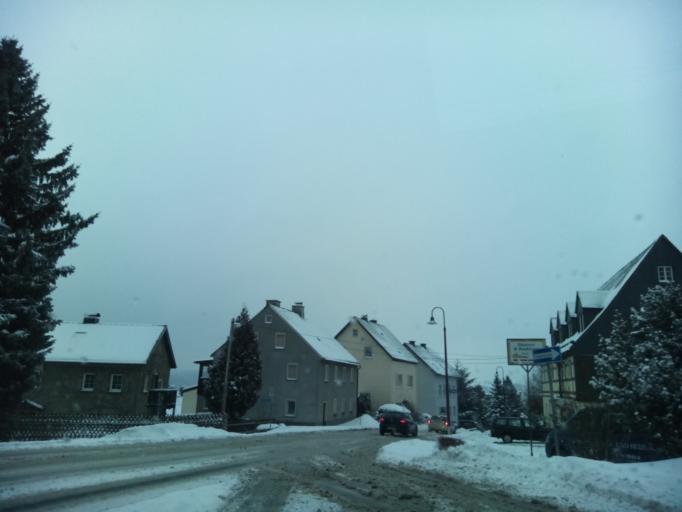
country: DE
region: Saxony
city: Grunhainichen
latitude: 50.7408
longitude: 13.1748
